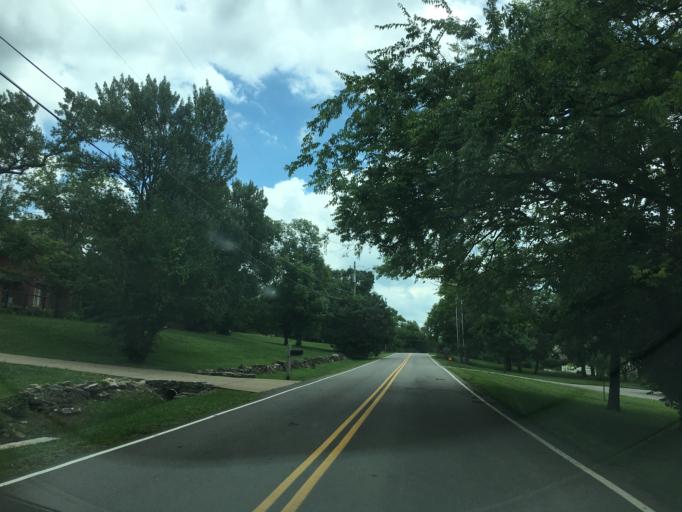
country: US
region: Tennessee
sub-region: Davidson County
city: Forest Hills
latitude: 36.0846
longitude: -86.8419
